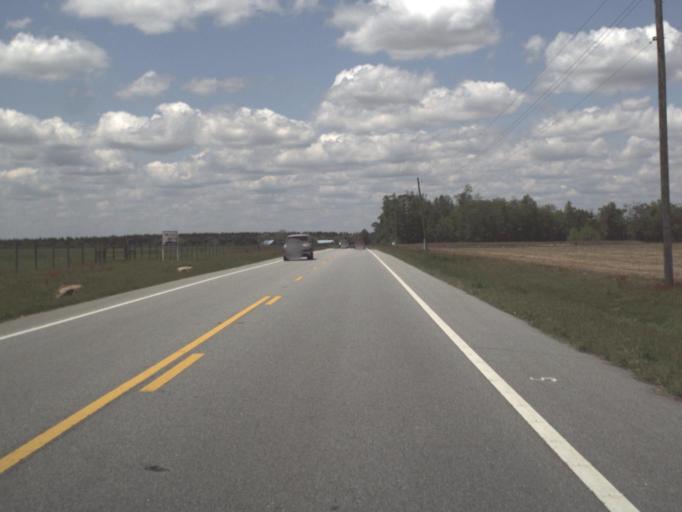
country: US
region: Florida
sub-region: Escambia County
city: Molino
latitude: 30.7452
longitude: -87.3672
